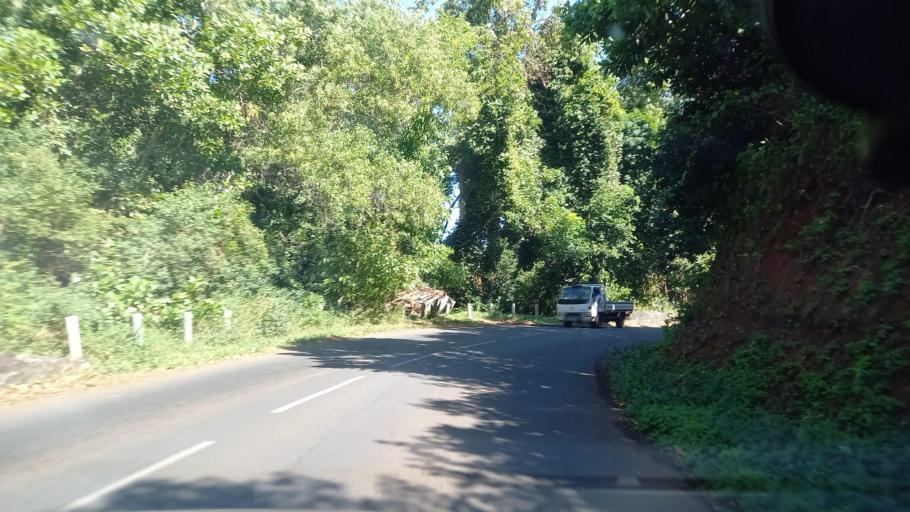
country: YT
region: Tsingoni
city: Tsingoni
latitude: -12.7864
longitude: 45.1530
